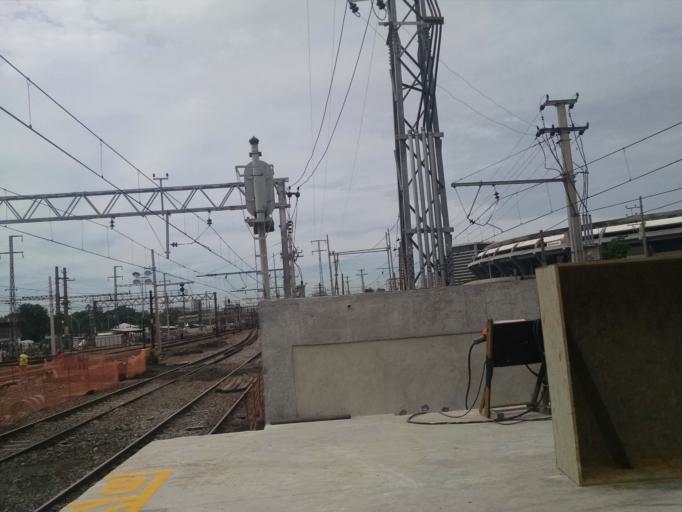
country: BR
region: Rio de Janeiro
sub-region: Rio De Janeiro
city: Rio de Janeiro
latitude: -22.9095
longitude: -43.2328
